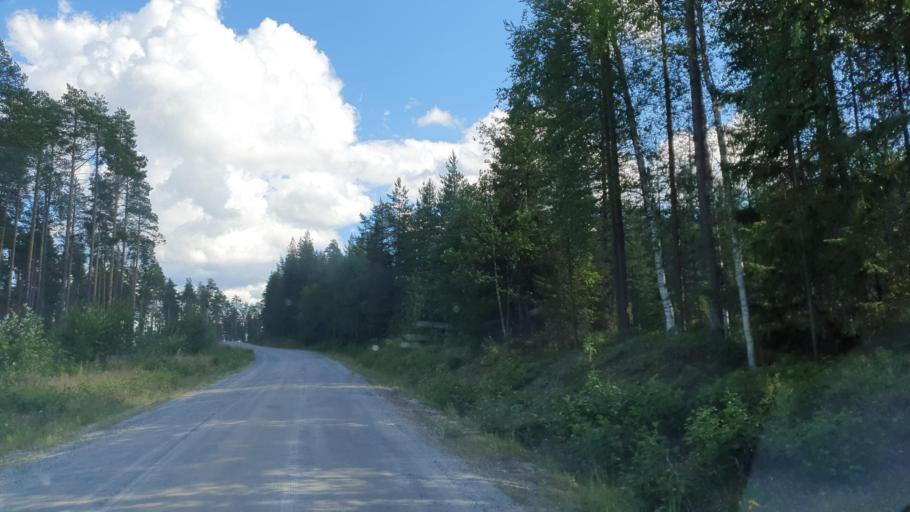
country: FI
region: Kainuu
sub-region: Kehys-Kainuu
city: Kuhmo
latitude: 64.0982
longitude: 29.4076
